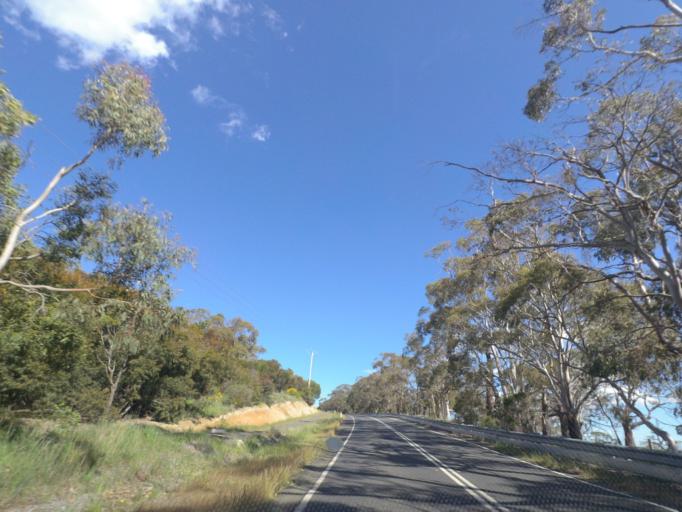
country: AU
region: Victoria
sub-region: Moorabool
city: Bacchus Marsh
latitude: -37.5698
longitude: 144.3123
